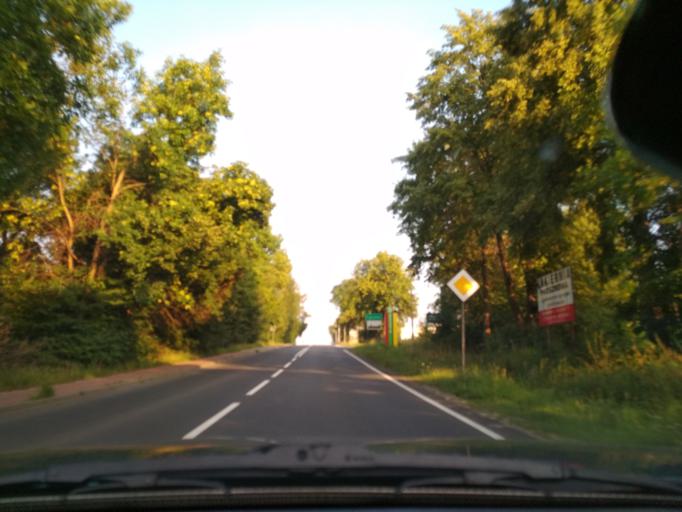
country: PL
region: Silesian Voivodeship
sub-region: Powiat zawiercianski
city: Ogrodzieniec
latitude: 50.4762
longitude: 19.4747
